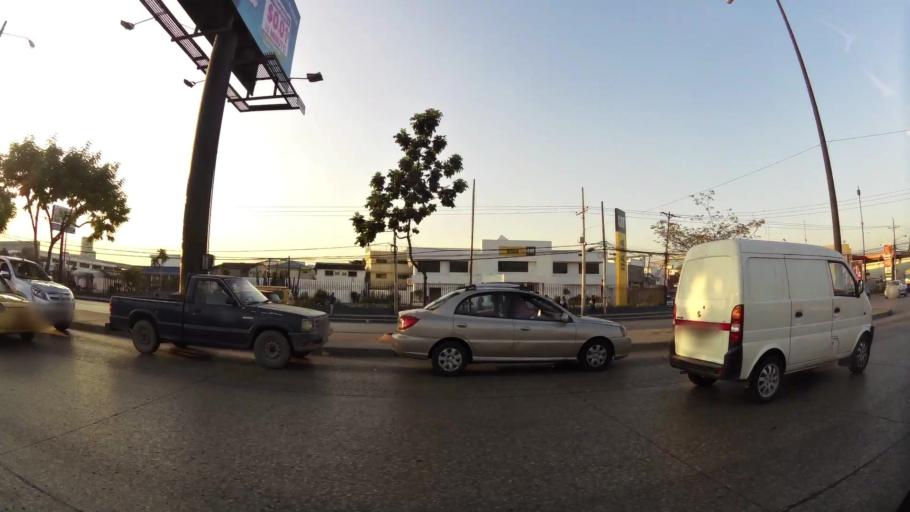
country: EC
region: Guayas
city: Guayaquil
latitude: -2.1478
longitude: -79.9063
